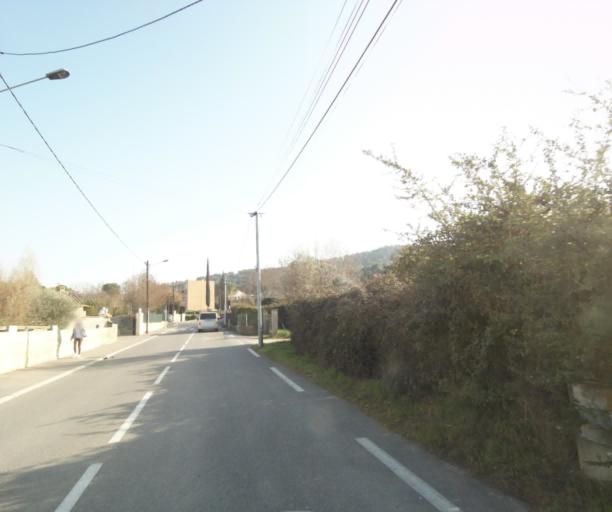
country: FR
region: Provence-Alpes-Cote d'Azur
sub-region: Departement des Bouches-du-Rhone
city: Les Pennes-Mirabeau
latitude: 43.4157
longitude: 5.2997
